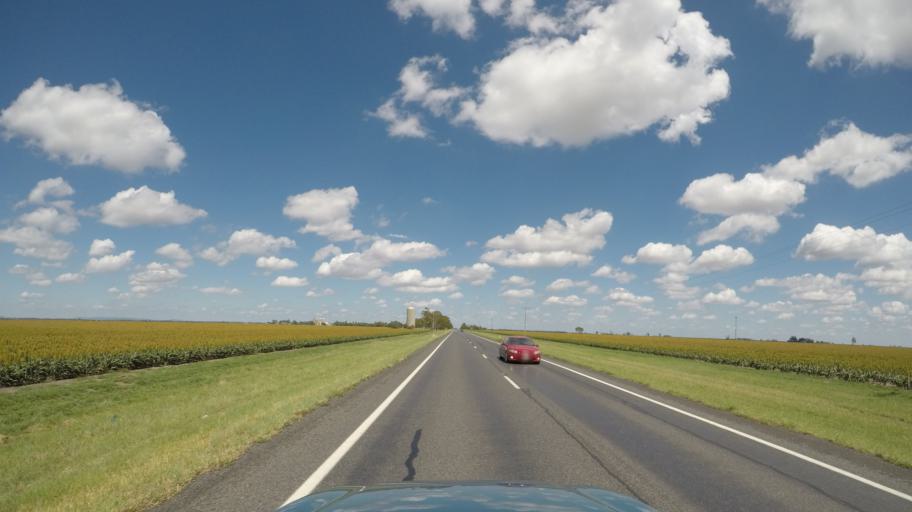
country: AU
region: Queensland
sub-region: Toowoomba
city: Oakey
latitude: -27.7571
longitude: 151.4656
